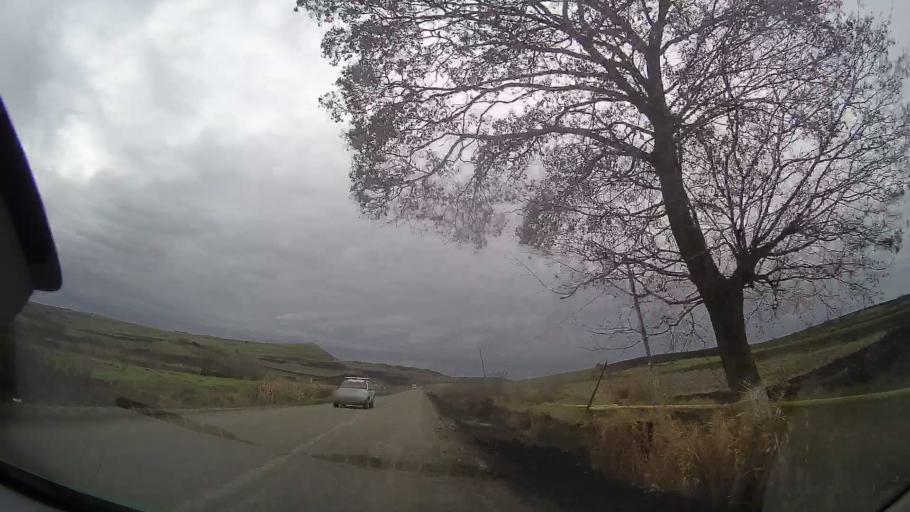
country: RO
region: Cluj
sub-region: Comuna Catina
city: Catina
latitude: 46.8169
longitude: 24.2248
